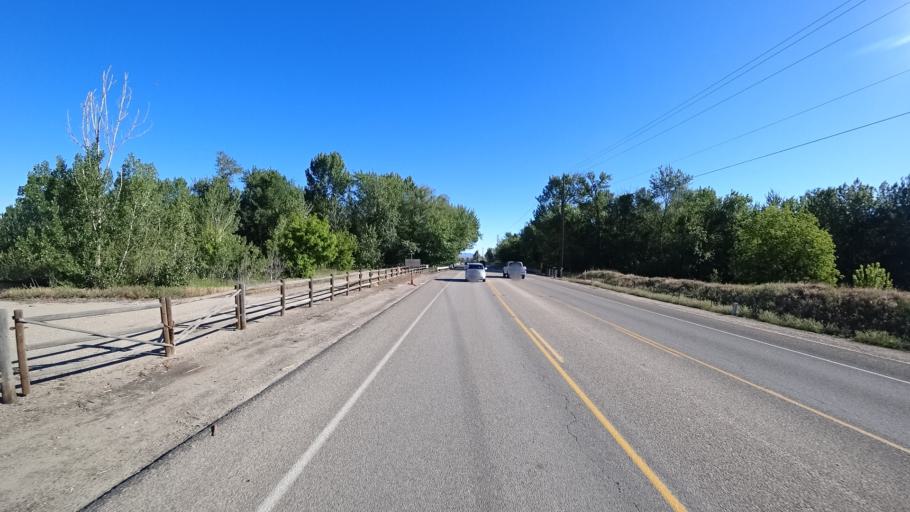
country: US
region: Idaho
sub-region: Ada County
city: Eagle
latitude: 43.6867
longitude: -116.4138
